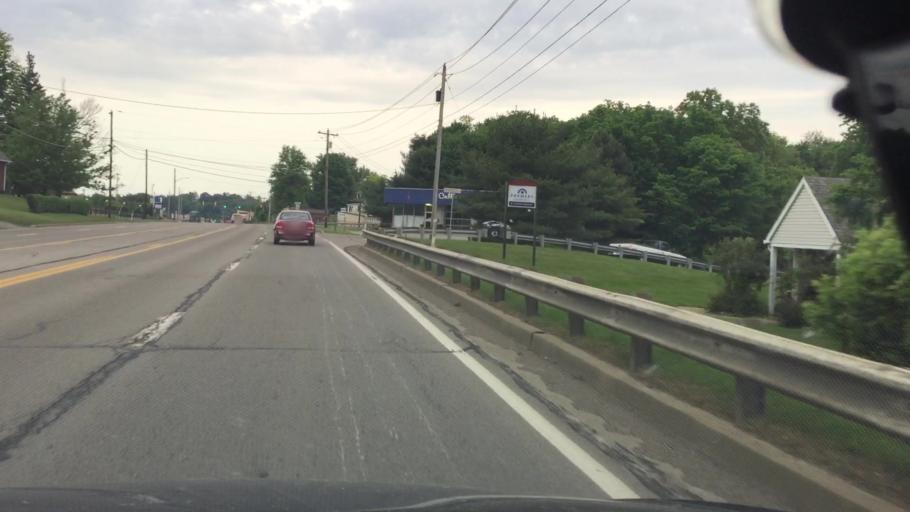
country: US
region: Pennsylvania
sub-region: Butler County
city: Homeacre-Lyndora
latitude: 40.8880
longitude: -79.9037
